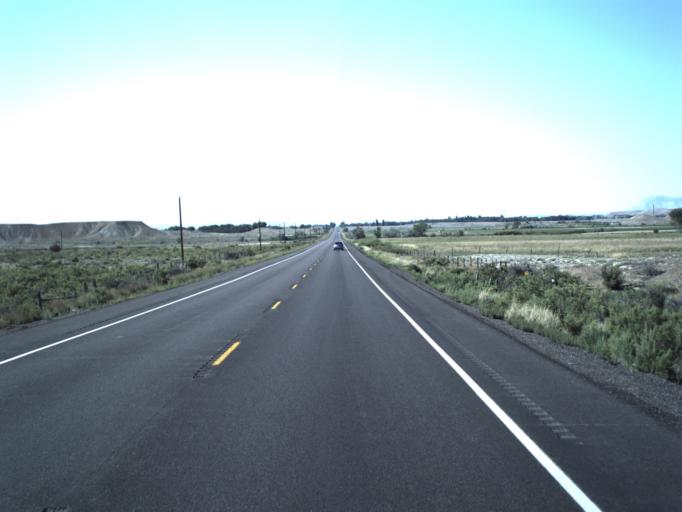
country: US
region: Utah
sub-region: Emery County
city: Huntington
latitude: 39.2787
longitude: -110.9760
